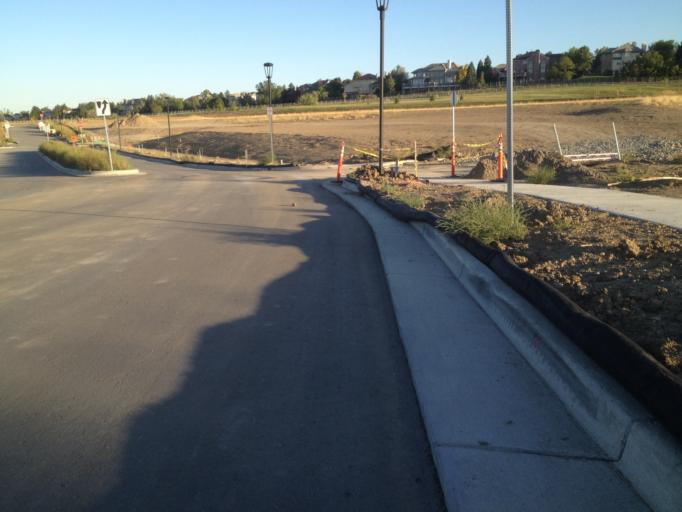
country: US
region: Colorado
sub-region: Boulder County
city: Superior
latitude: 39.9490
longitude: -105.1611
